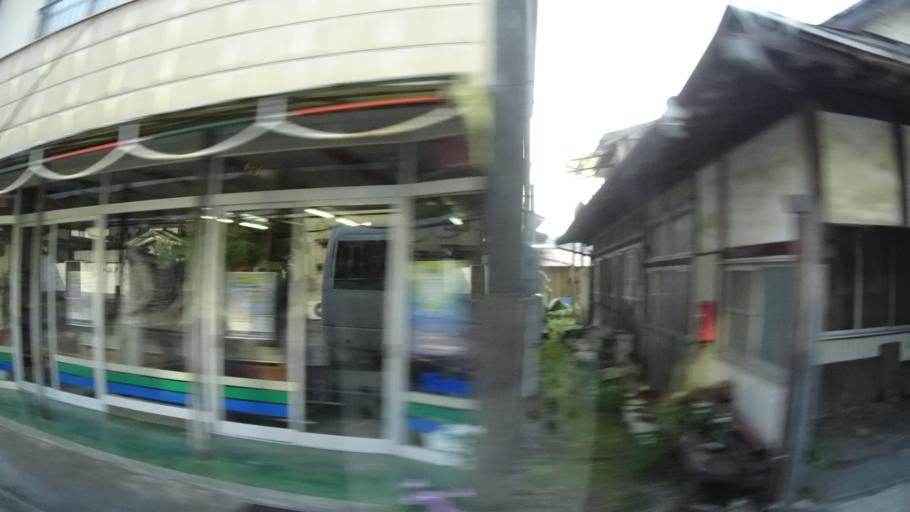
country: JP
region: Tochigi
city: Karasuyama
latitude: 36.5779
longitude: 140.1062
